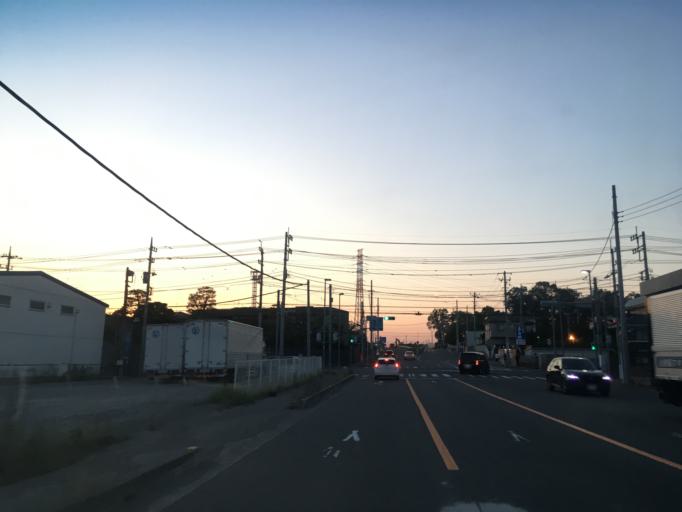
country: JP
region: Saitama
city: Tokorozawa
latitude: 35.7971
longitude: 139.5022
